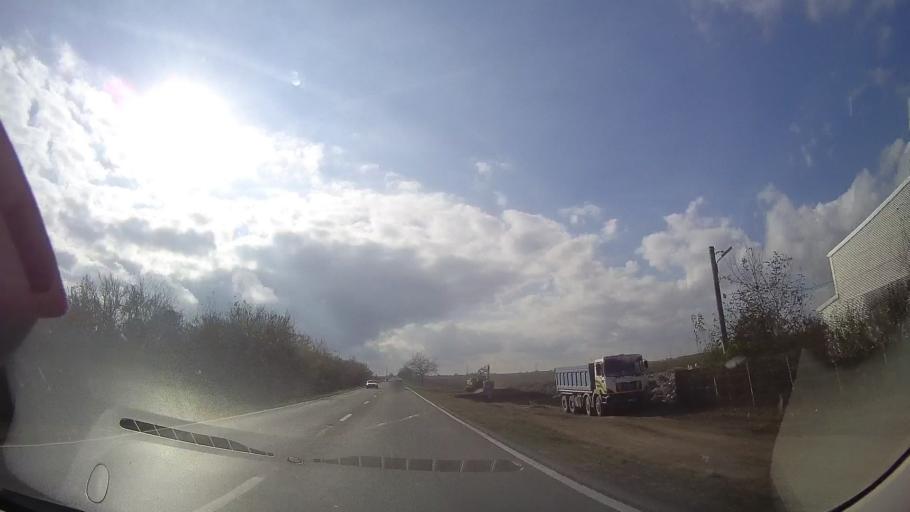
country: RO
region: Constanta
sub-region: Comuna Agigea
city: Agigea
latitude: 44.0817
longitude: 28.6046
